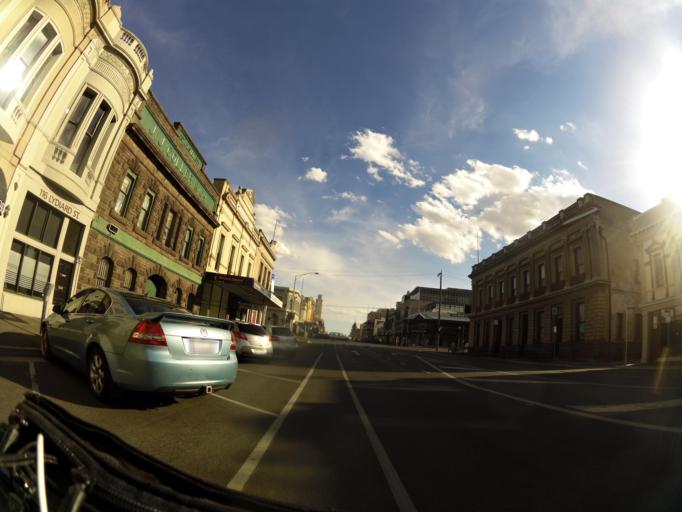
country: AU
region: Victoria
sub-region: Ballarat North
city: Ballarat Central
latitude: -37.5592
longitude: 143.8583
